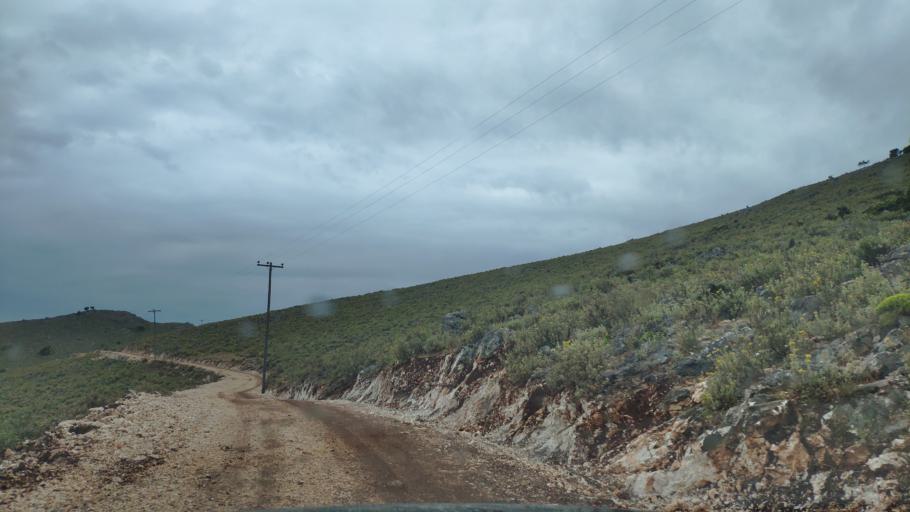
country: GR
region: West Greece
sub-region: Nomos Aitolias kai Akarnanias
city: Archontochorion
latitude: 38.6892
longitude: 21.0369
